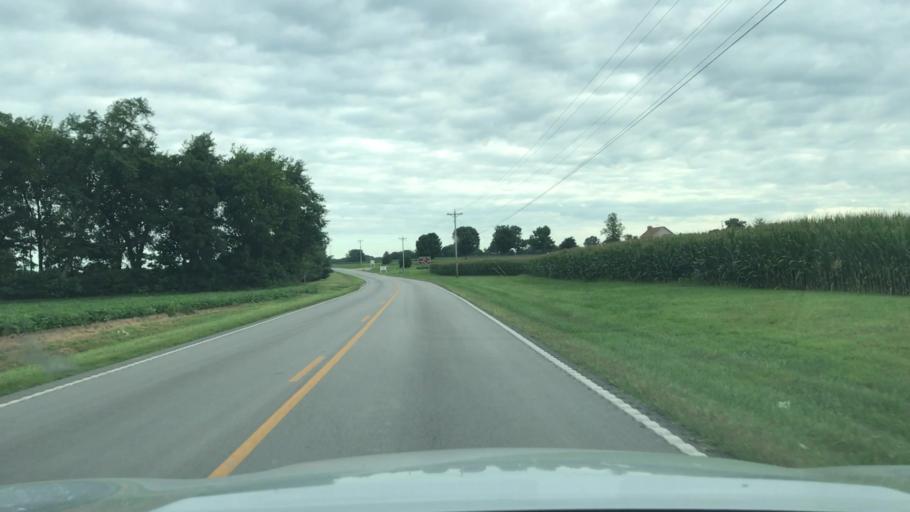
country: US
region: Kentucky
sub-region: Todd County
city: Guthrie
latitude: 36.6686
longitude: -87.1977
